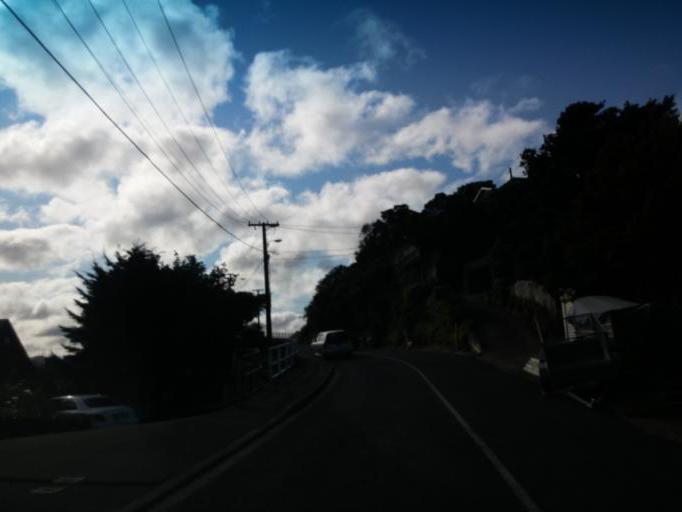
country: NZ
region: Wellington
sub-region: Wellington City
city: Wellington
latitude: -41.3202
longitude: 174.8208
